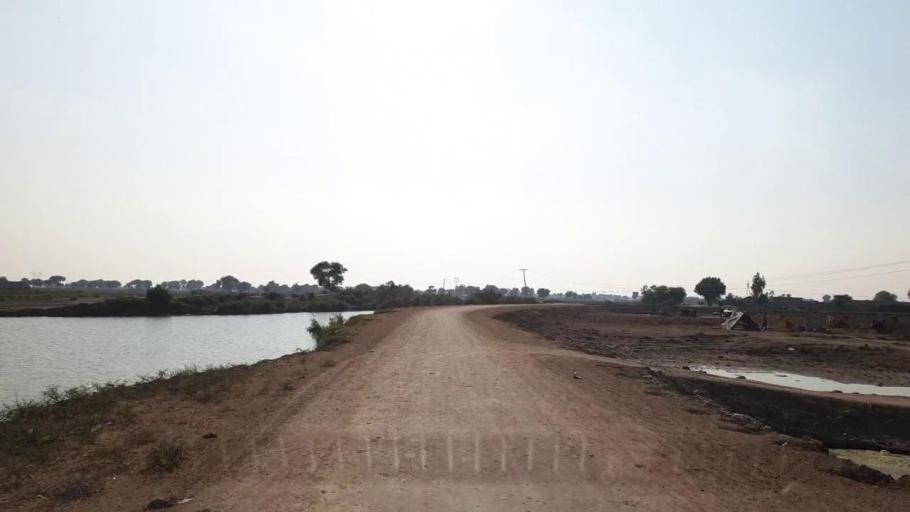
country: PK
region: Sindh
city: Sehwan
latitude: 26.4419
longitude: 67.8085
